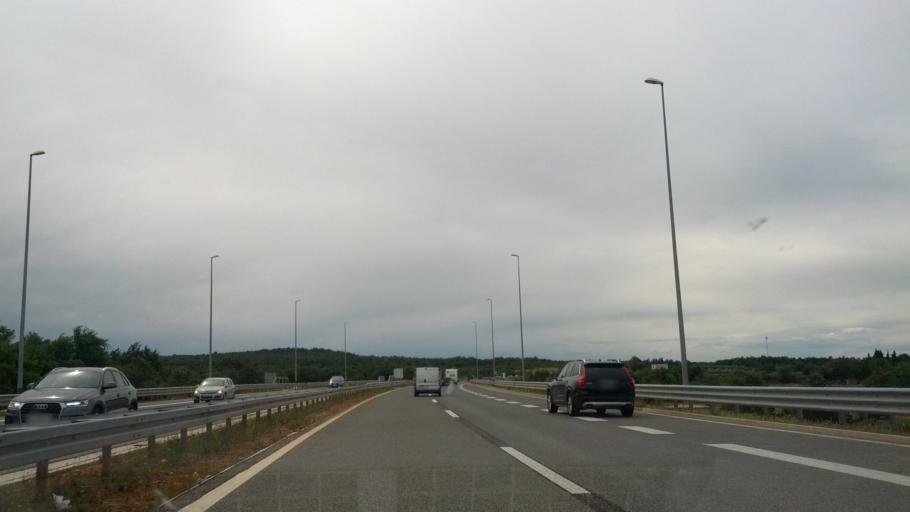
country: HR
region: Istarska
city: Karojba
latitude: 45.2377
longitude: 13.7179
